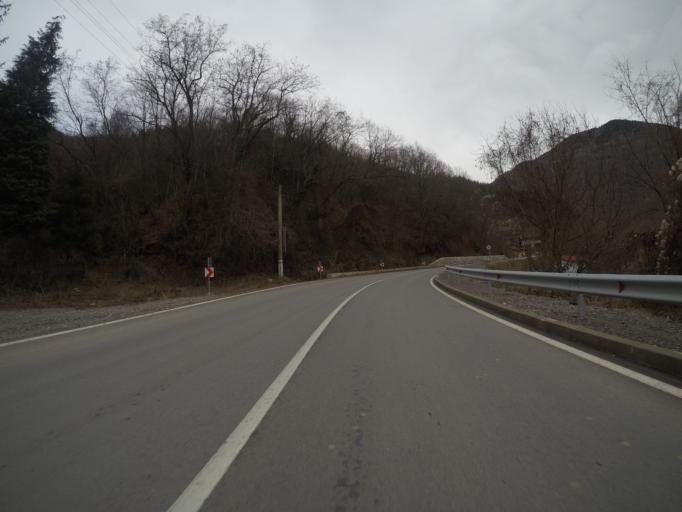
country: BG
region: Kyustendil
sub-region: Obshtina Rila
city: Rila
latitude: 42.1272
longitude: 23.2351
